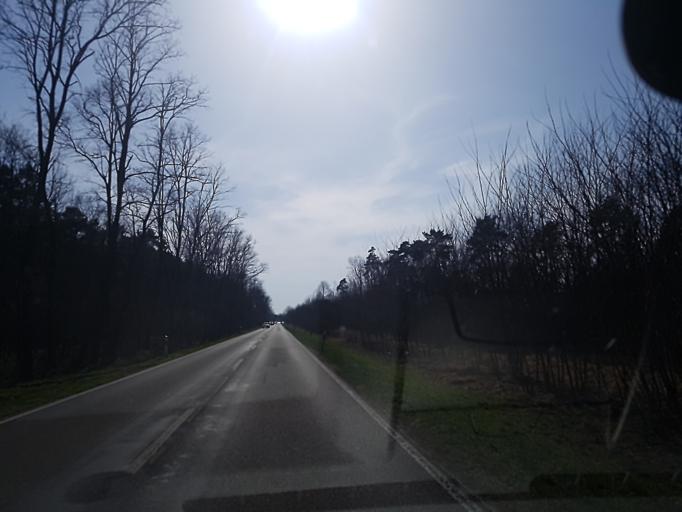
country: DE
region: Brandenburg
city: Calau
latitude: 51.7671
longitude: 14.0156
